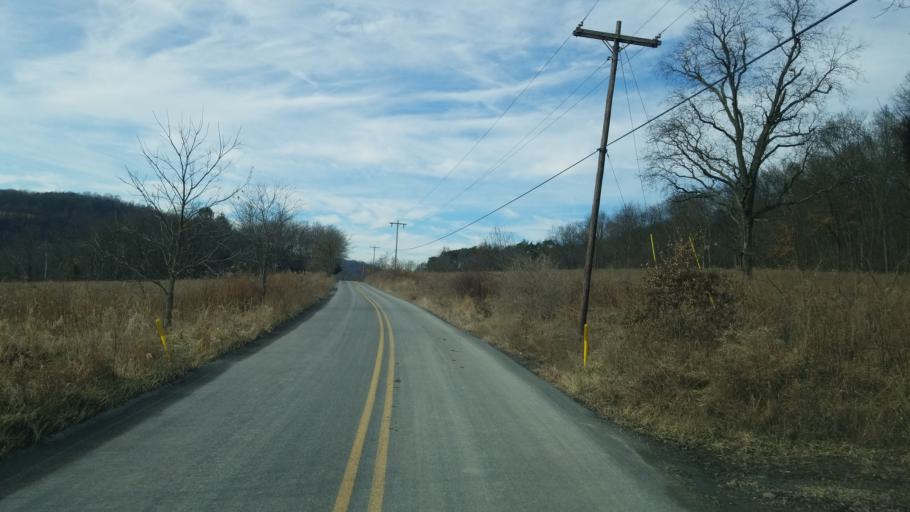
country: US
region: Pennsylvania
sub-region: Jefferson County
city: Punxsutawney
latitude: 40.8435
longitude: -79.1352
